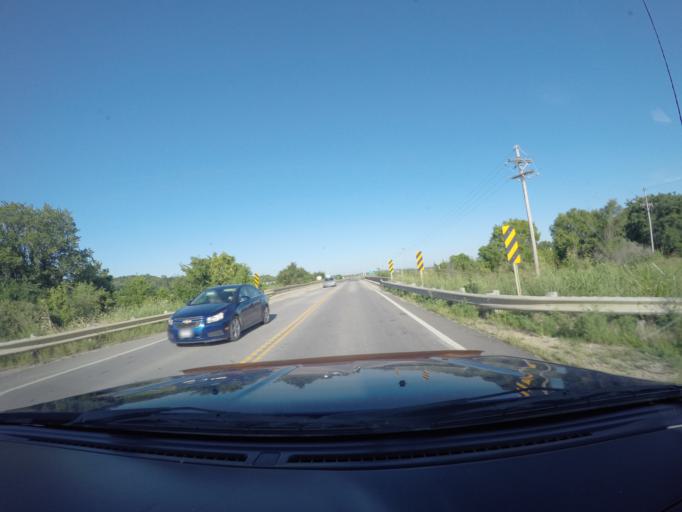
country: US
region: Kansas
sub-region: Douglas County
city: Lawrence
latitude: 39.0669
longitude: -95.3363
